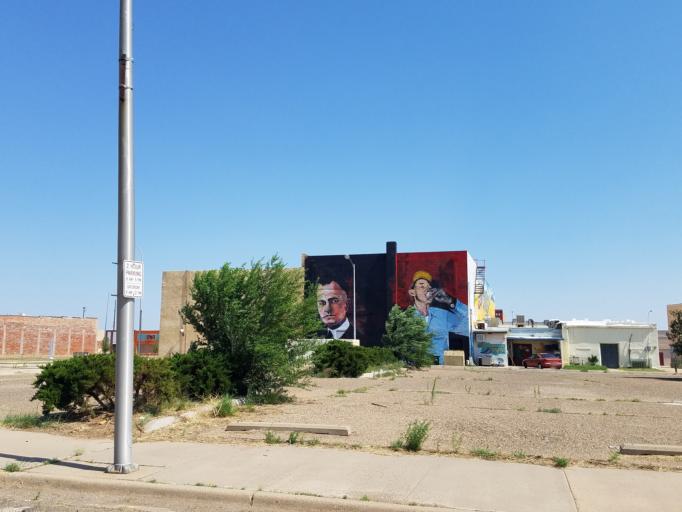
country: US
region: New Mexico
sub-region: Quay County
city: Tucumcari
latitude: 35.1780
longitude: -103.7250
